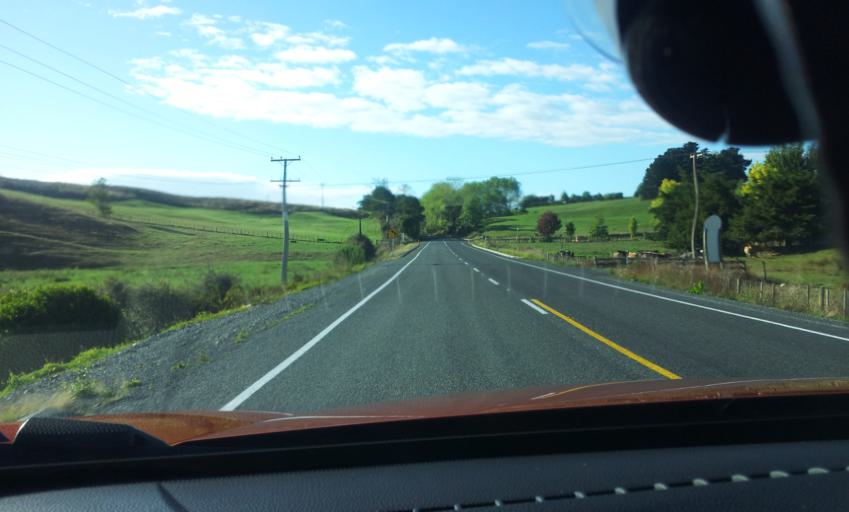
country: NZ
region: Waikato
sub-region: Hauraki District
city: Ngatea
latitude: -37.3116
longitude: 175.3838
